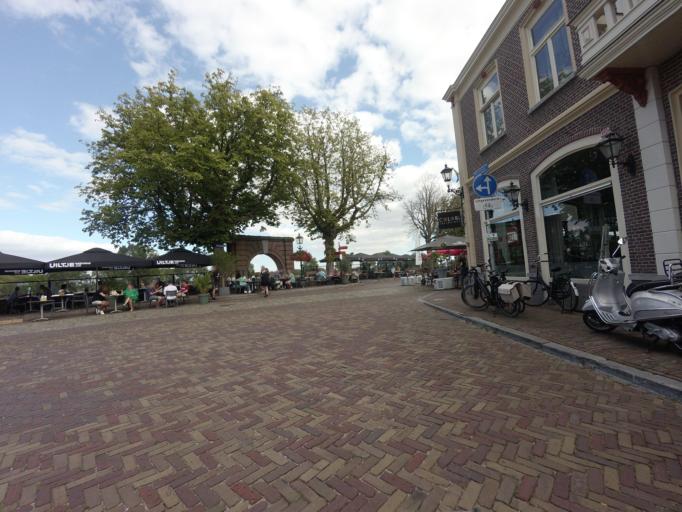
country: NL
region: North Brabant
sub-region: Gemeente Grave
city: Grave
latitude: 51.7607
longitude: 5.7412
